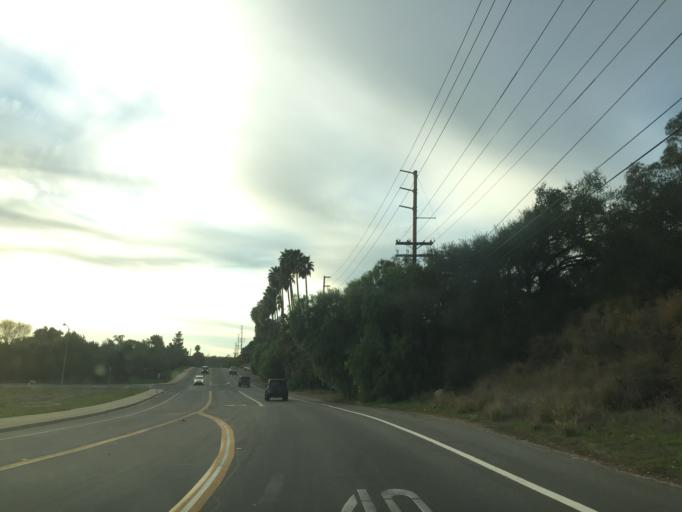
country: US
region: California
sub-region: Santa Barbara County
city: Goleta
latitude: 34.4515
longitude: -119.7913
